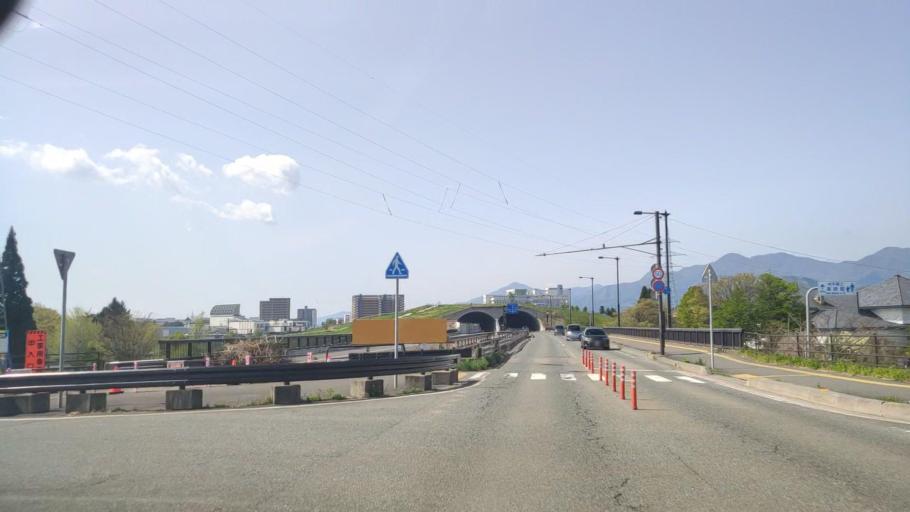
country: JP
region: Iwate
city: Morioka-shi
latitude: 39.6953
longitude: 141.1285
